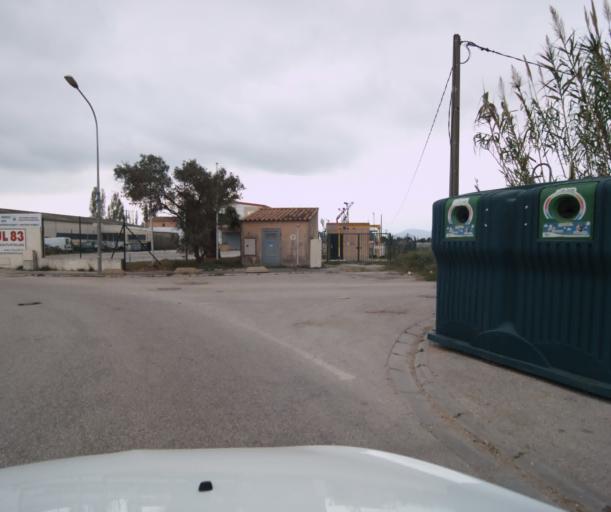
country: FR
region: Provence-Alpes-Cote d'Azur
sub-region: Departement du Var
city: La Crau
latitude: 43.1337
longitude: 6.0700
